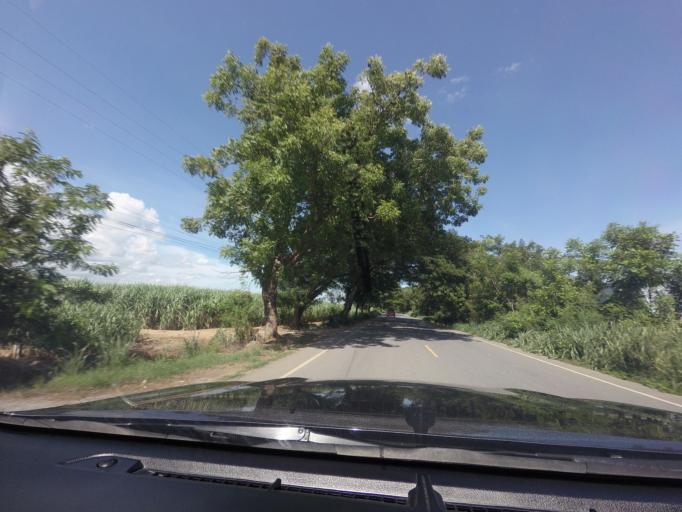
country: TH
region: Kanchanaburi
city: Phanom Thuan
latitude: 14.1684
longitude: 99.8345
